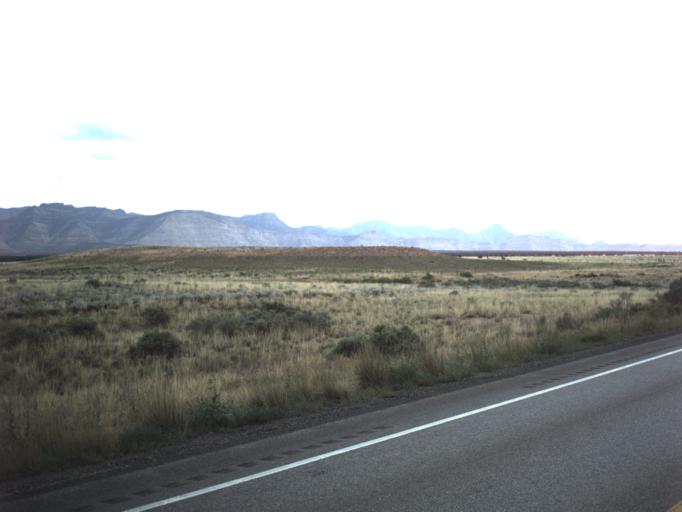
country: US
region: Utah
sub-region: Carbon County
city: East Carbon City
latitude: 39.4414
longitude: -110.4646
